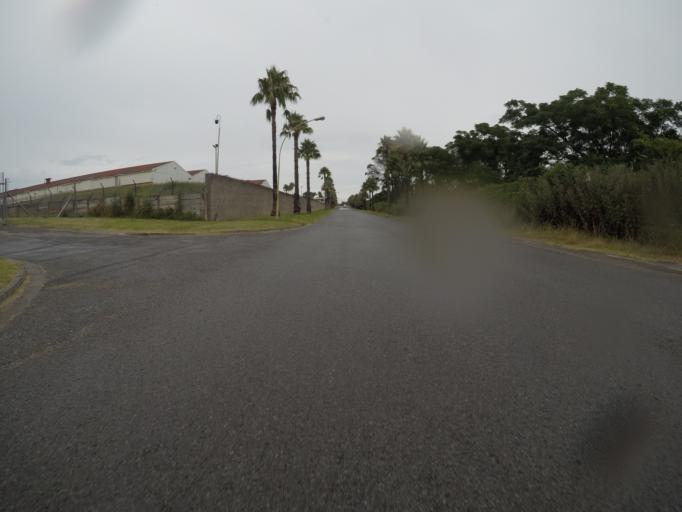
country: ZA
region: Eastern Cape
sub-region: Buffalo City Metropolitan Municipality
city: East London
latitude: -32.9707
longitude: 27.8188
